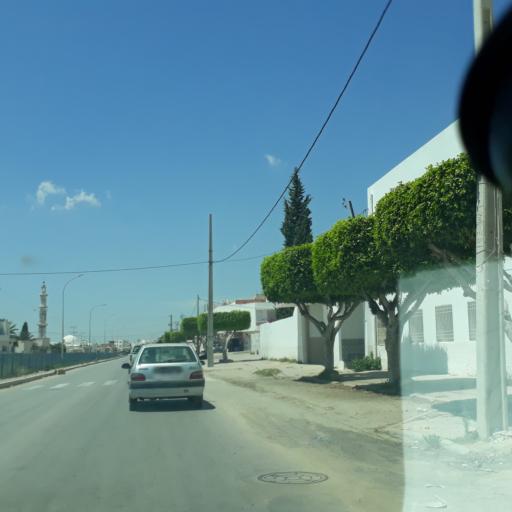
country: TN
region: Safaqis
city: Al Qarmadah
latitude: 34.8061
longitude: 10.7555
